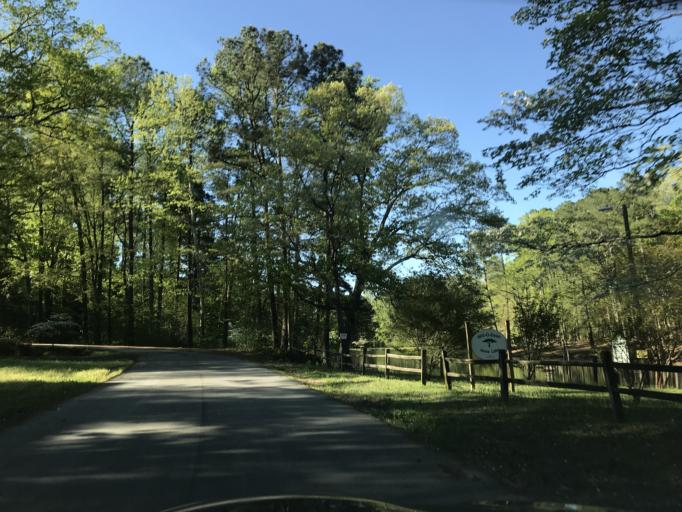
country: US
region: North Carolina
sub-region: Wake County
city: Knightdale
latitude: 35.8579
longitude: -78.5607
